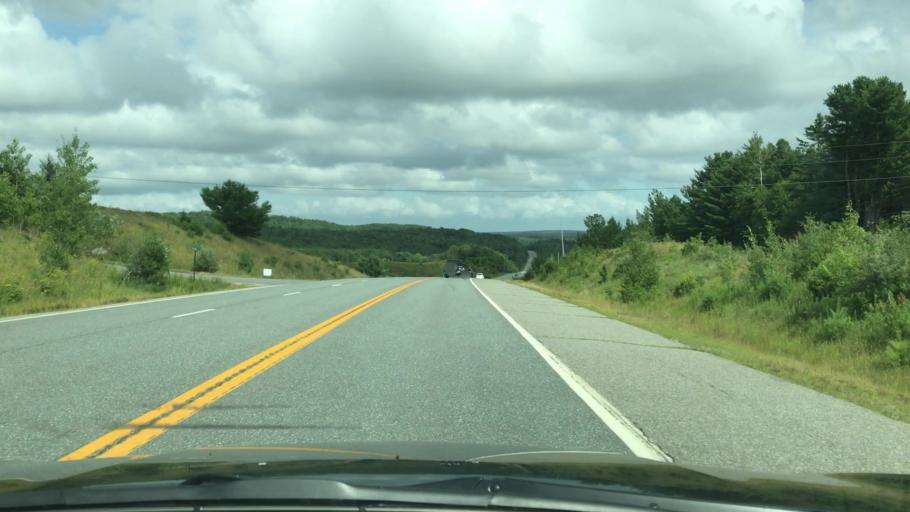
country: US
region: Maine
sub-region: Hancock County
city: Orland
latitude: 44.5678
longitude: -68.6241
